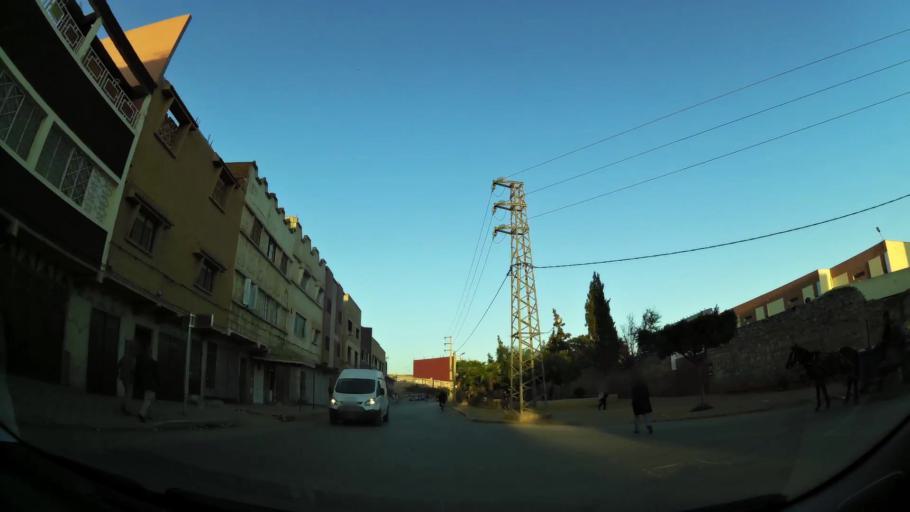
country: MA
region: Oriental
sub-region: Berkane-Taourirt
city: Berkane
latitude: 34.9183
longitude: -2.3265
